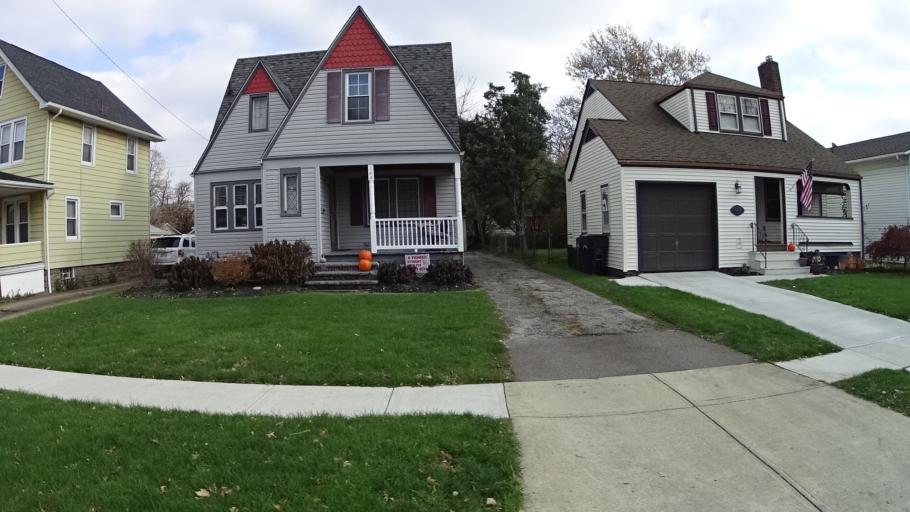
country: US
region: Ohio
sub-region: Lorain County
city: Elyria
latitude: 41.3758
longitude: -82.0882
